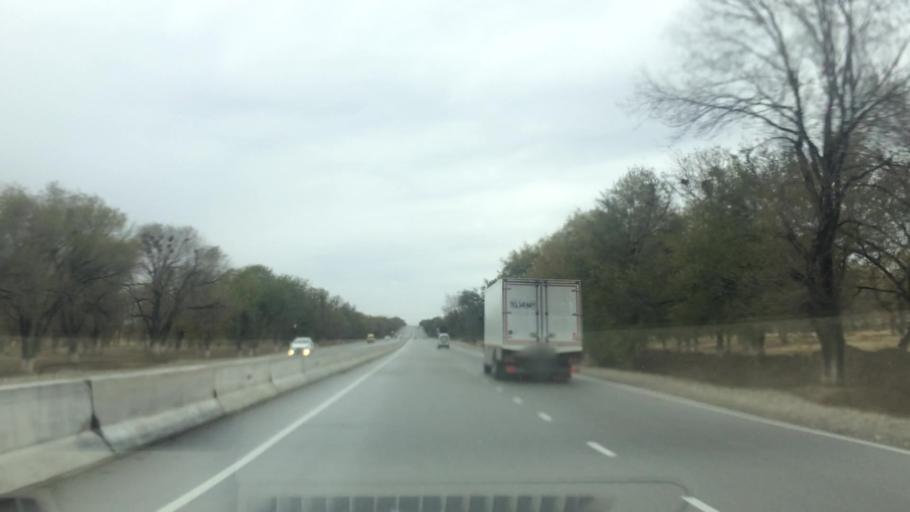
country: UZ
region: Samarqand
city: Bulung'ur
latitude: 39.8986
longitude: 67.4996
